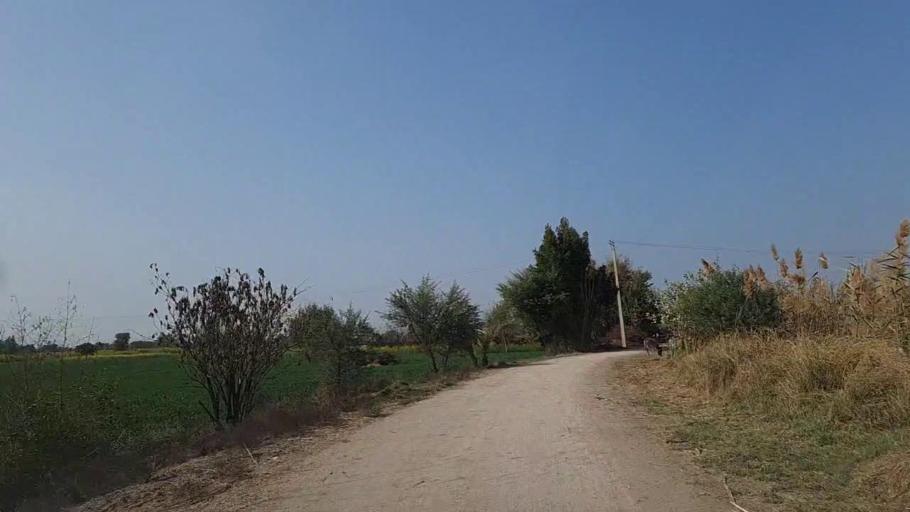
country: PK
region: Sindh
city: Jam Sahib
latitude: 26.2888
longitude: 68.5651
